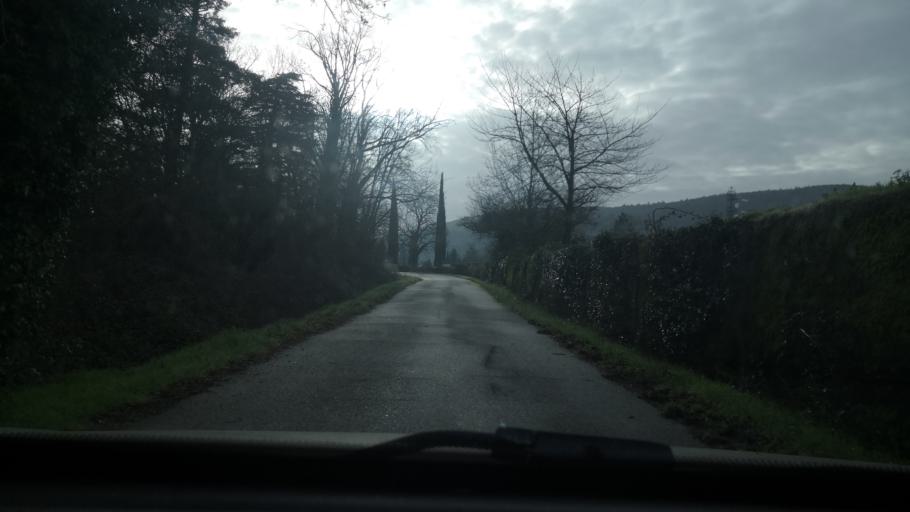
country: FR
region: Rhone-Alpes
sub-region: Departement de la Drome
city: Dieulefit
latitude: 44.5222
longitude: 5.0539
